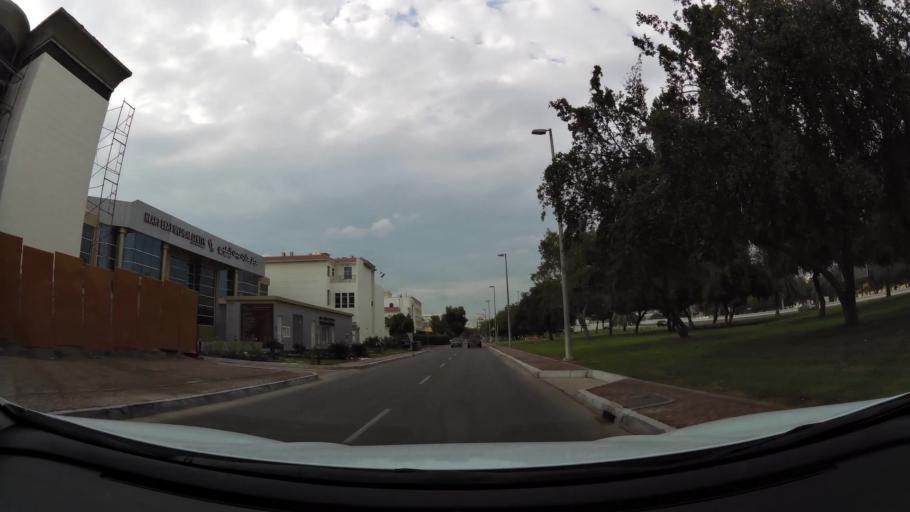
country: AE
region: Abu Dhabi
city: Abu Dhabi
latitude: 24.4436
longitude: 54.3948
